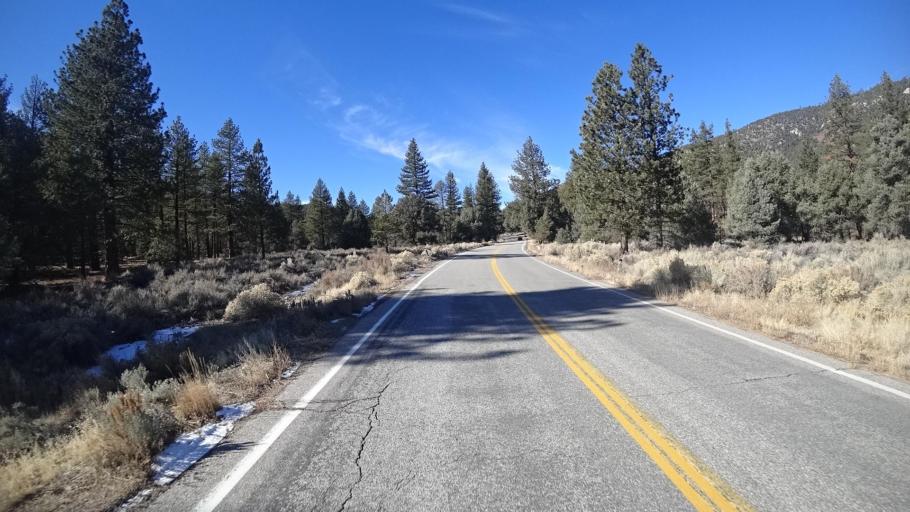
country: US
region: California
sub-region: Kern County
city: Pine Mountain Club
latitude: 34.8531
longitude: -119.1808
